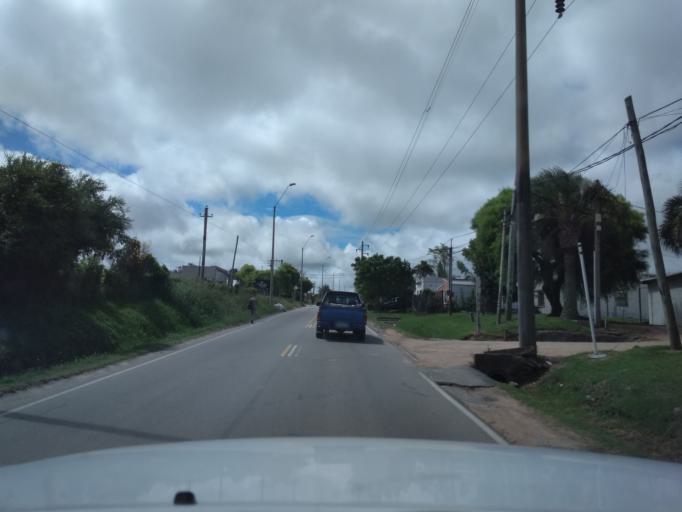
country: UY
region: Canelones
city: Pando
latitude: -34.7067
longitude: -55.9652
